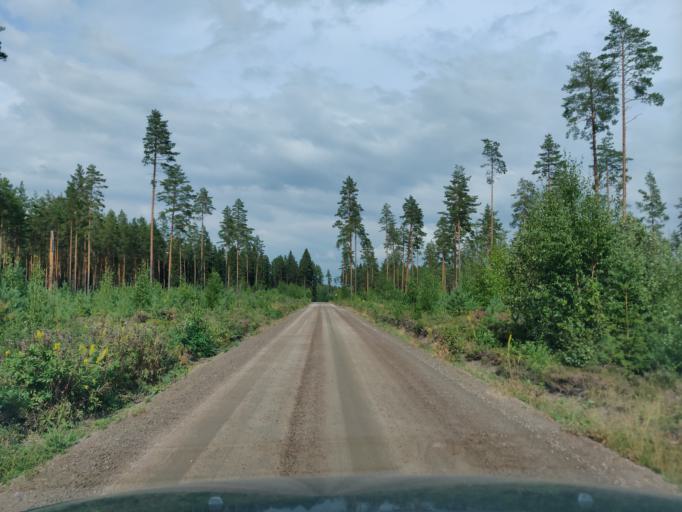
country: SE
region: Vaermland
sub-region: Hagfors Kommun
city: Hagfors
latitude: 59.9840
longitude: 13.5560
